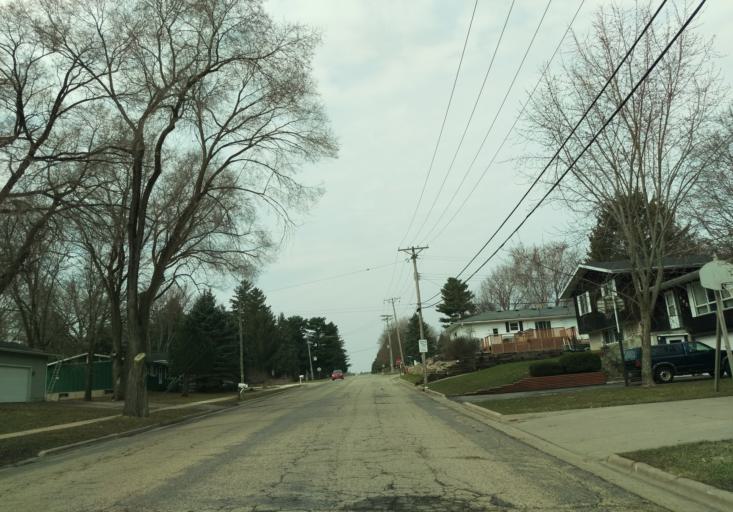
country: US
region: Wisconsin
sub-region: Columbia County
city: Lodi
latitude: 43.3125
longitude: -89.5348
